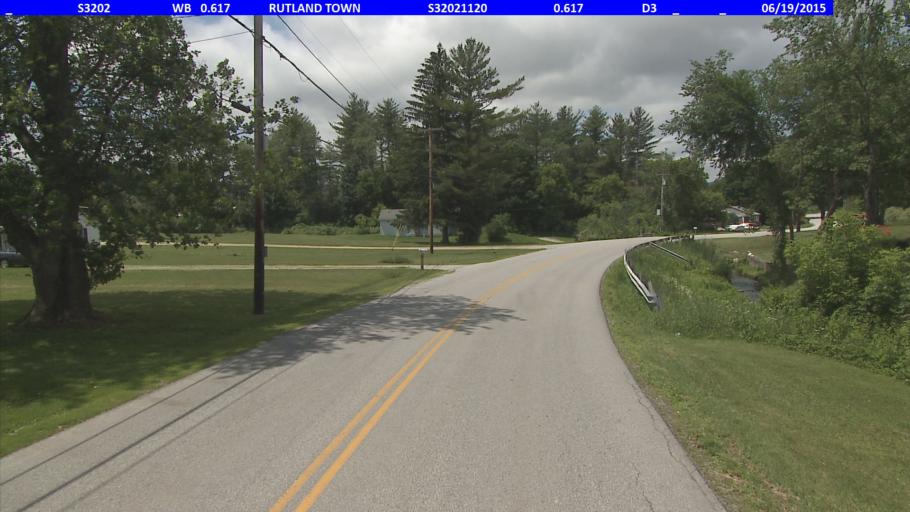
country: US
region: Vermont
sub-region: Rutland County
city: Rutland
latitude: 43.5872
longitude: -72.9576
